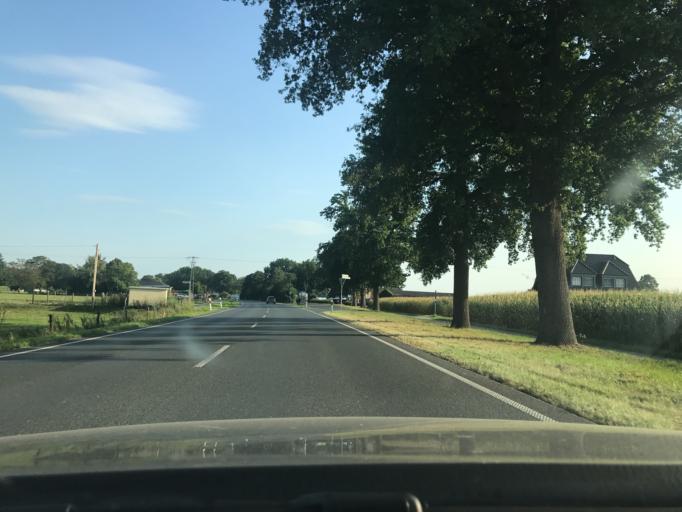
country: DE
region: North Rhine-Westphalia
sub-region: Regierungsbezirk Dusseldorf
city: Kevelaer
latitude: 51.5471
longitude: 6.2674
